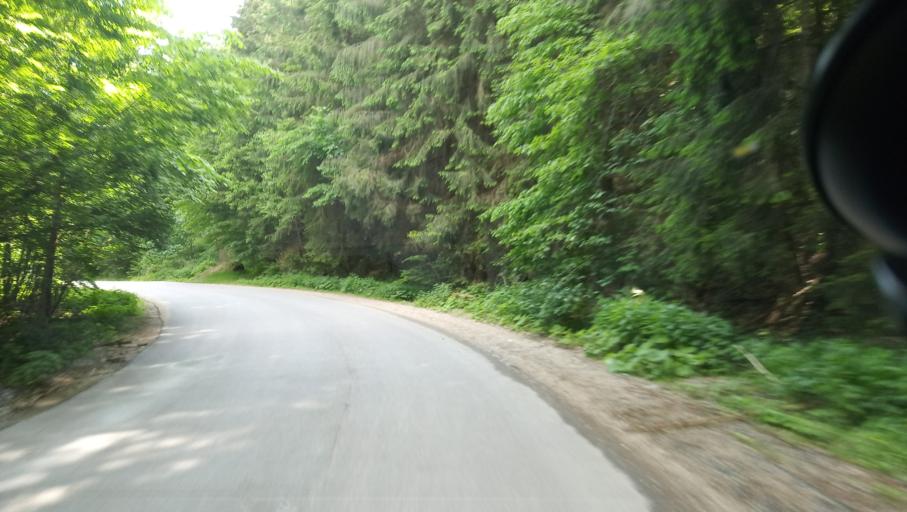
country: RO
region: Cluj
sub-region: Comuna Maguri-Racatau
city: Maguri-Racatau
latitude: 46.7088
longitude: 23.2485
